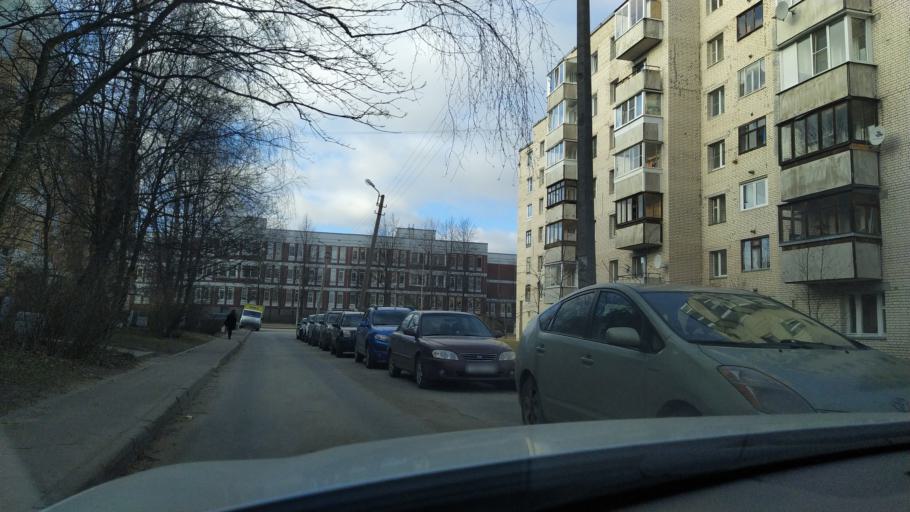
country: RU
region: St.-Petersburg
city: Pushkin
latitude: 59.7361
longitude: 30.4030
